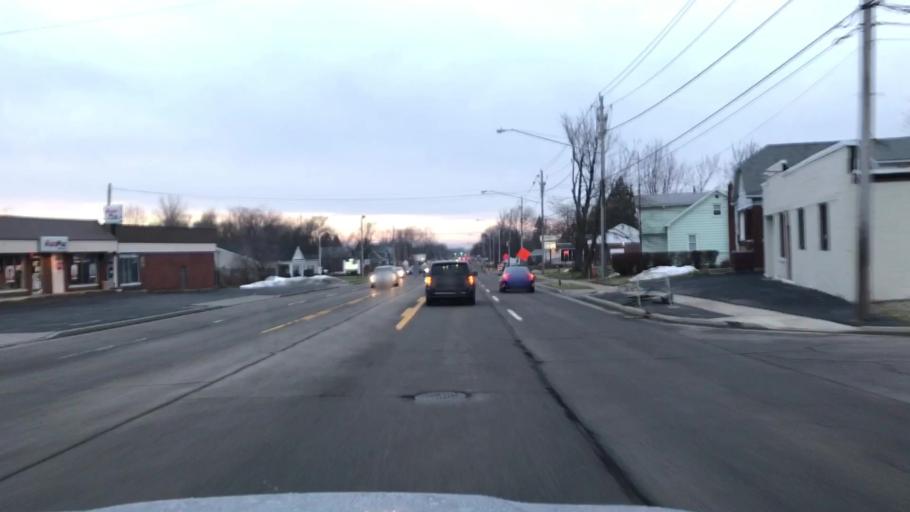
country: US
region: New York
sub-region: Erie County
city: Blasdell
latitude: 42.8008
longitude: -78.7961
